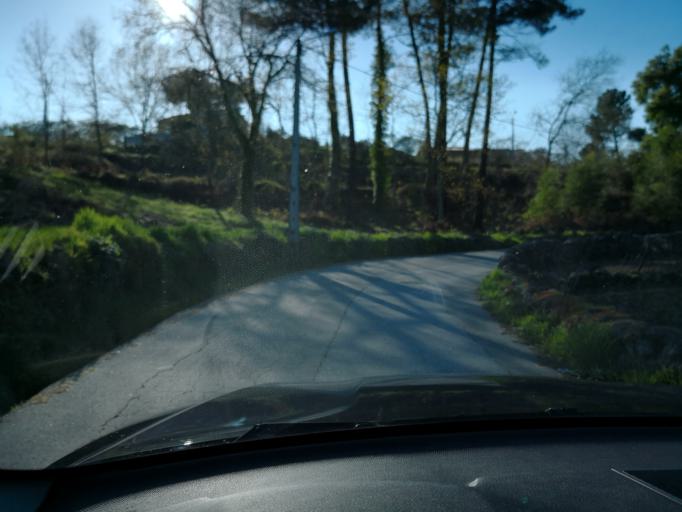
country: PT
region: Vila Real
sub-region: Vila Real
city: Vila Real
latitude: 41.2915
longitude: -7.7760
